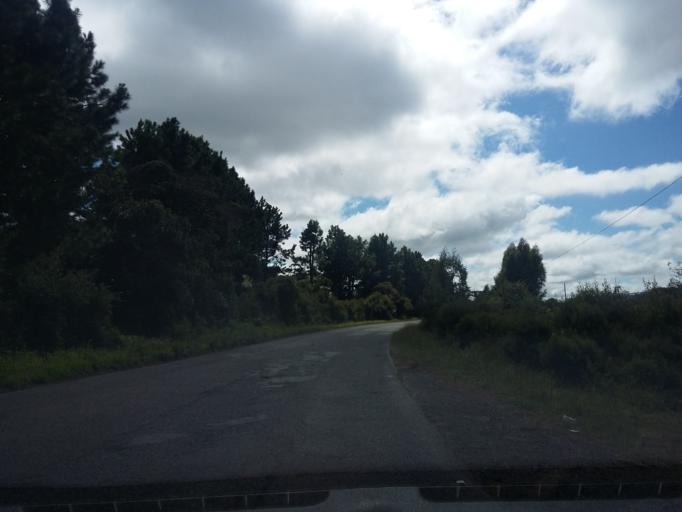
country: BR
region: Santa Catarina
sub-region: Sao Joaquim
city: Sao Joaquim
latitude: -28.2401
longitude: -49.8798
